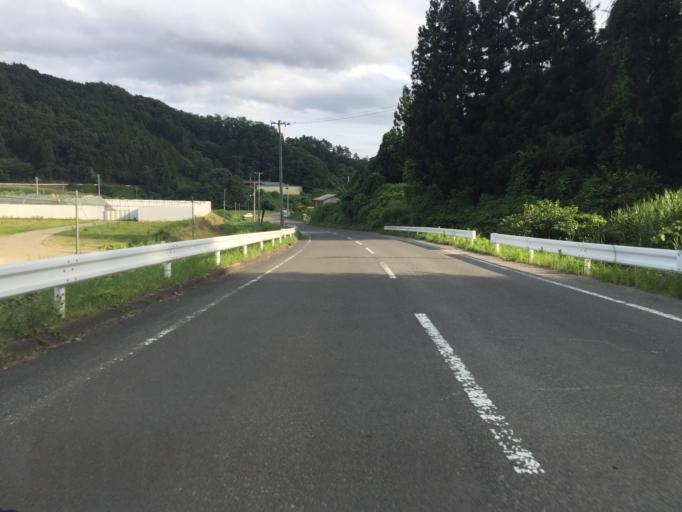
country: JP
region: Fukushima
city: Fukushima-shi
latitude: 37.6951
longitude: 140.5722
